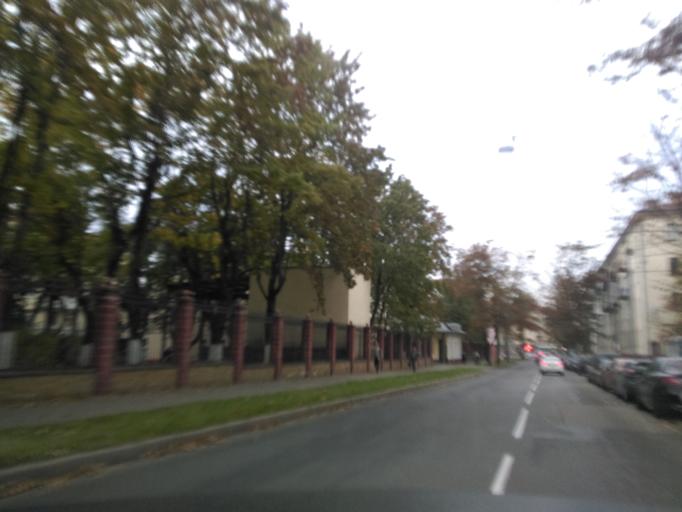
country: BY
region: Minsk
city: Minsk
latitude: 53.9108
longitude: 27.5827
